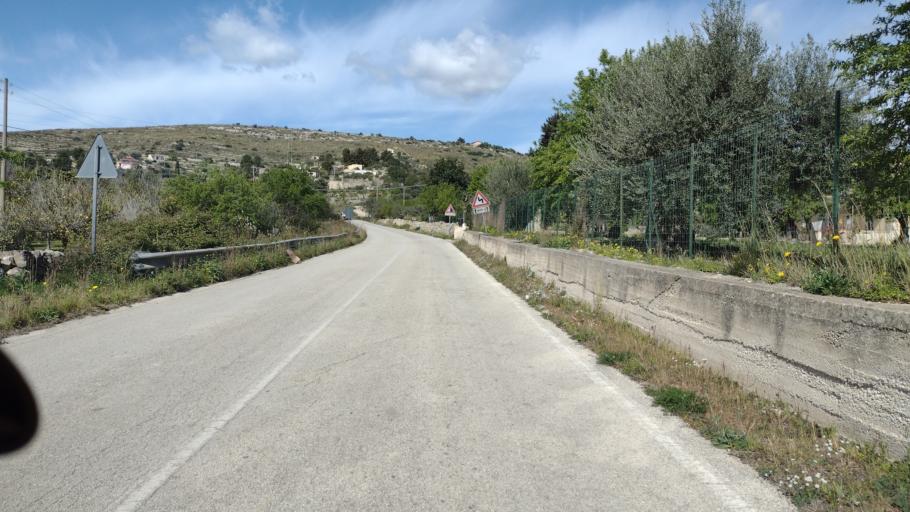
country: IT
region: Sicily
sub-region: Provincia di Siracusa
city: Noto
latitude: 36.9070
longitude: 15.0315
